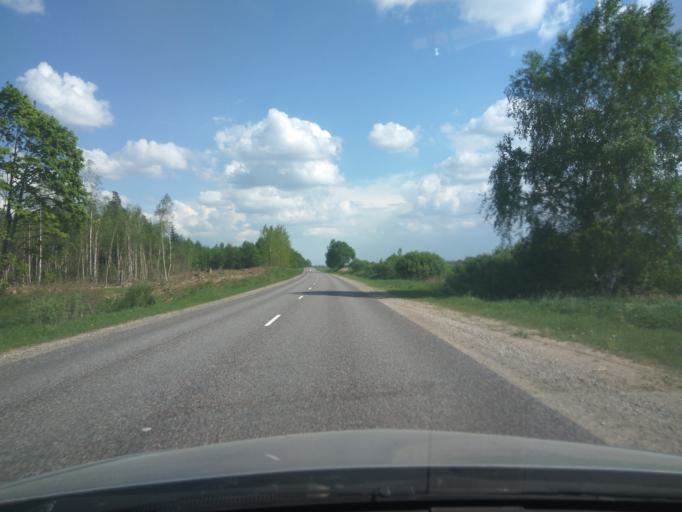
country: LV
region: Kuldigas Rajons
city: Kuldiga
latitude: 57.0313
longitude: 21.8457
